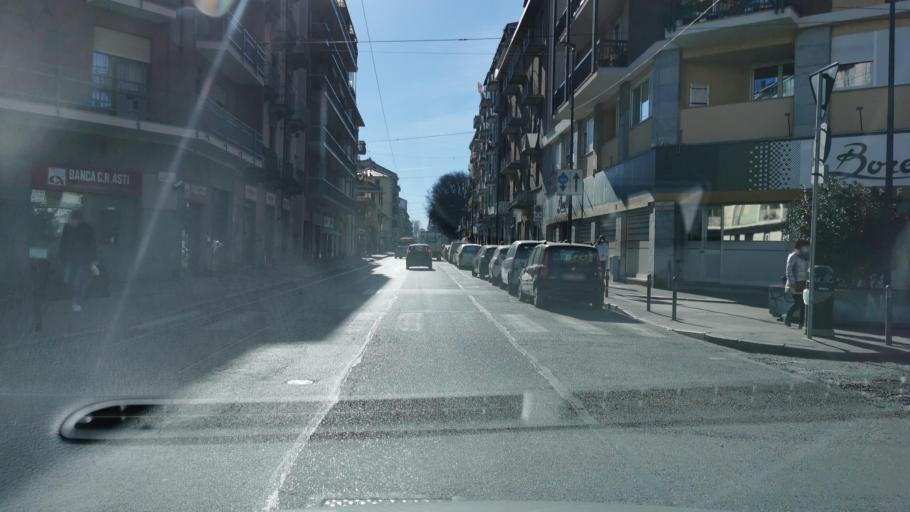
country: IT
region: Piedmont
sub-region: Provincia di Torino
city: Turin
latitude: 45.0966
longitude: 7.6795
